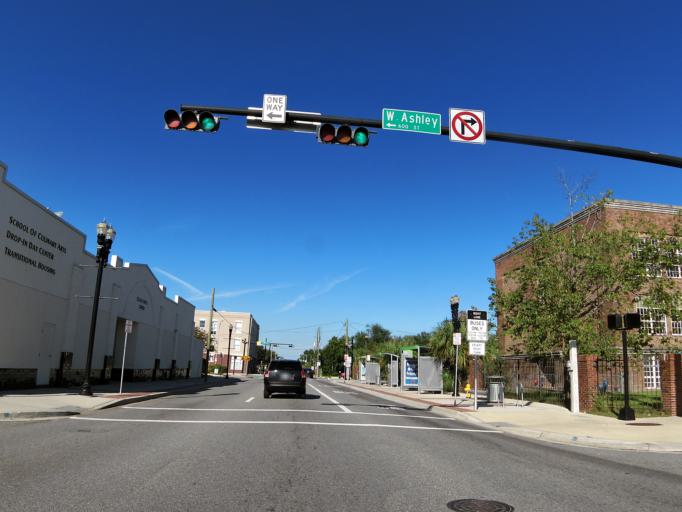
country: US
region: Florida
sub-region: Duval County
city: Jacksonville
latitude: 30.3323
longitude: -81.6640
